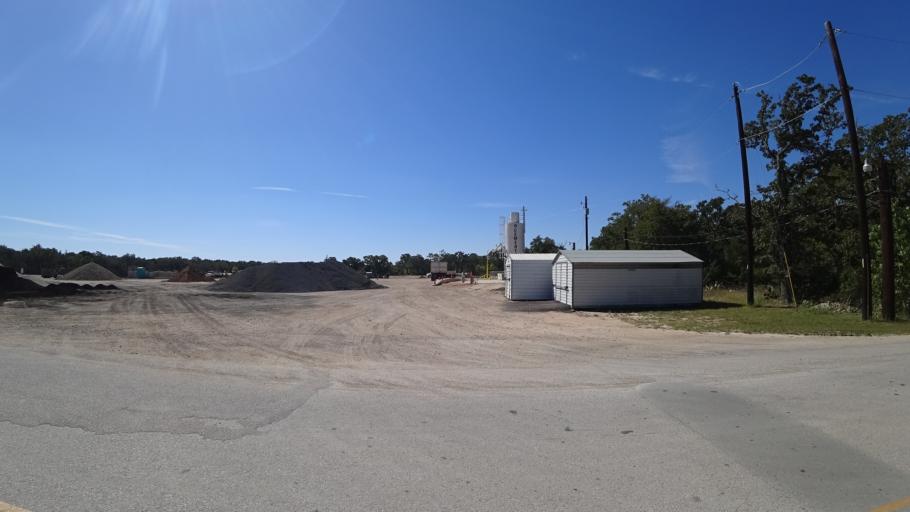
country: US
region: Texas
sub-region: Travis County
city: Hornsby Bend
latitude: 30.2751
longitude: -97.6088
